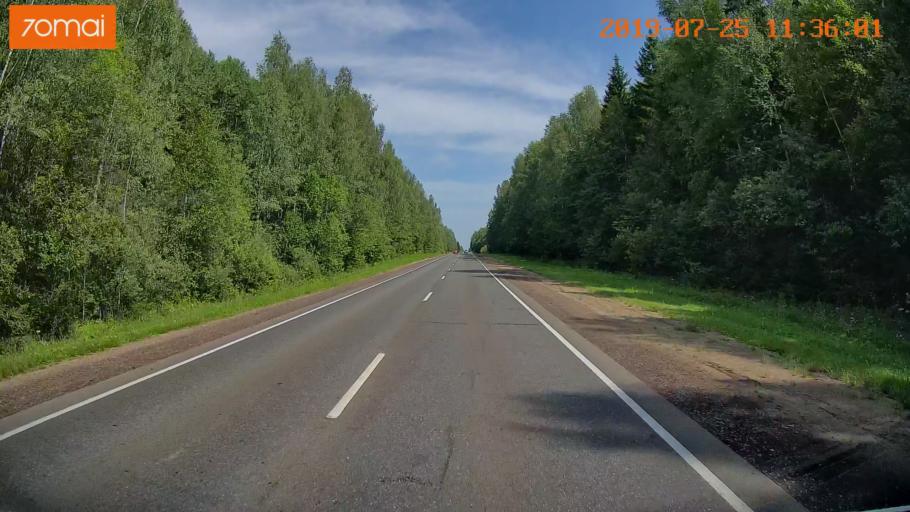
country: RU
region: Ivanovo
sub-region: Privolzhskiy Rayon
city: Ples
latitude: 57.4184
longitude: 41.4404
